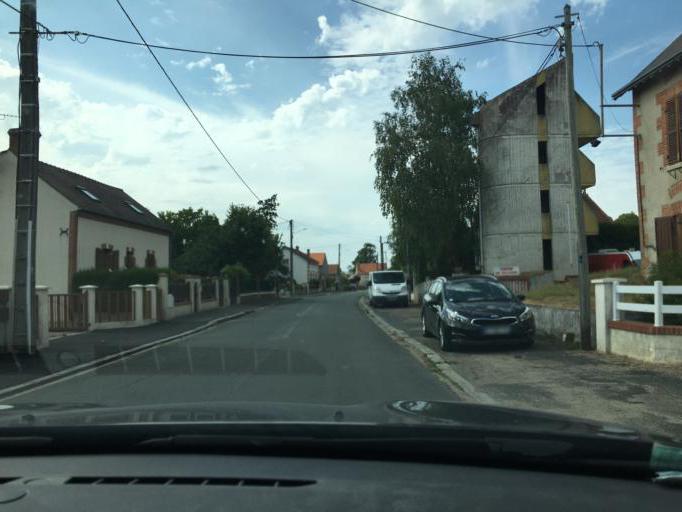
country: FR
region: Centre
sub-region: Departement du Loiret
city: Jargeau
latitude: 47.8627
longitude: 2.1264
